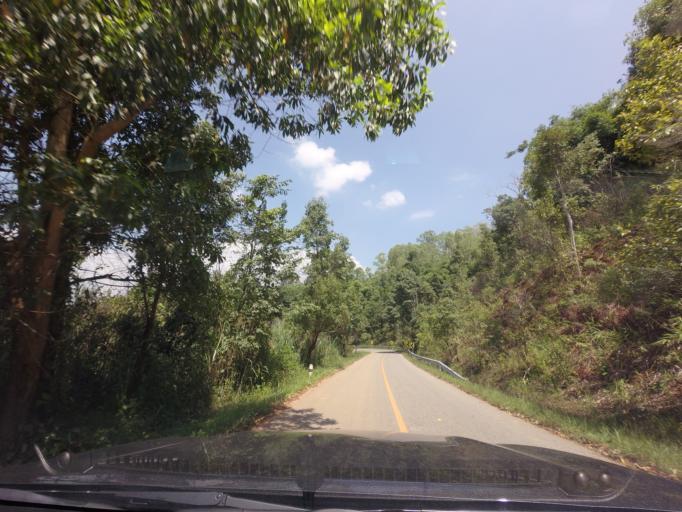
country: TH
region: Loei
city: Na Haeo
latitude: 17.6010
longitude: 100.8987
